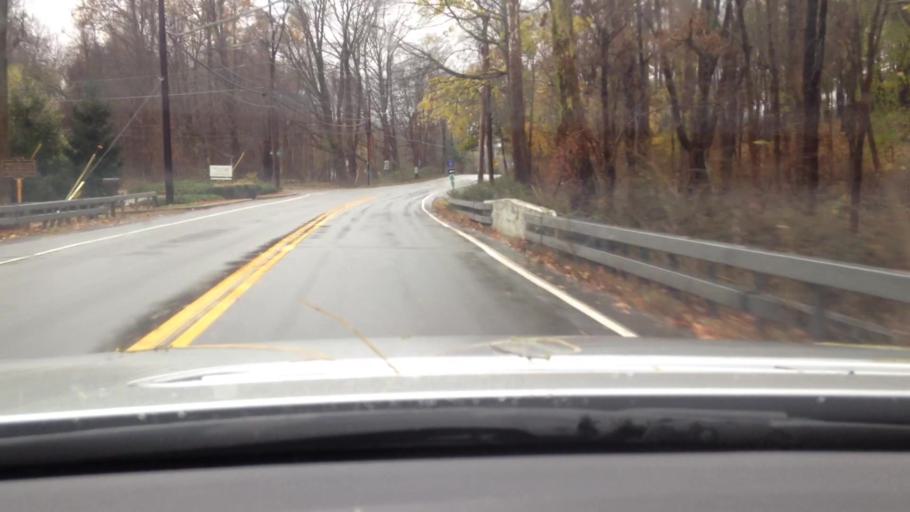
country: US
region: New York
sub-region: Orange County
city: West Point
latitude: 41.3859
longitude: -73.9348
